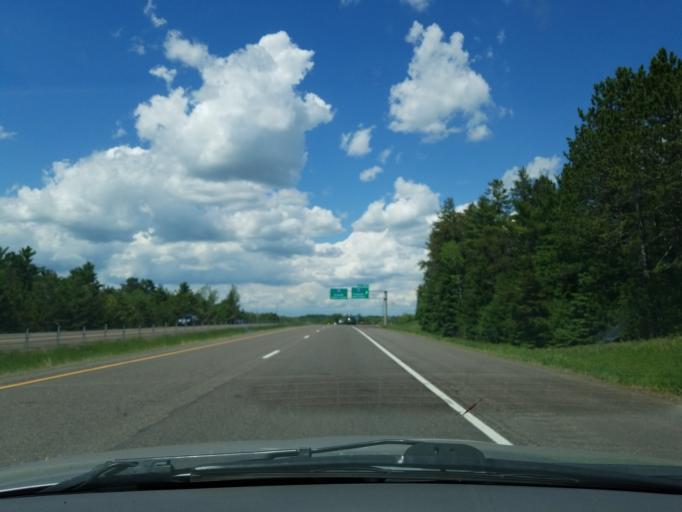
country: US
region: Minnesota
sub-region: Carlton County
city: Cloquet
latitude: 46.6834
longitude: -92.4601
